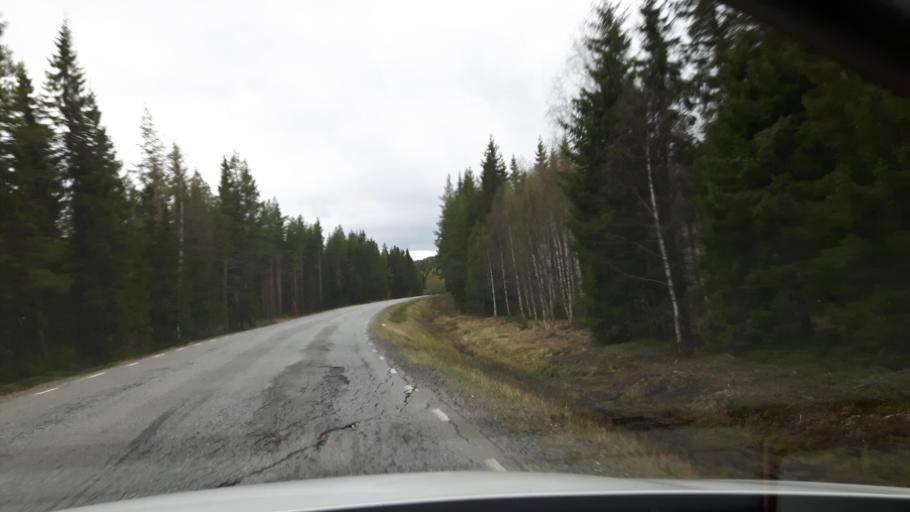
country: SE
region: Vaesterbotten
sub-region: Skelleftea Kommun
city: Burtraesk
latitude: 64.2969
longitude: 20.5271
